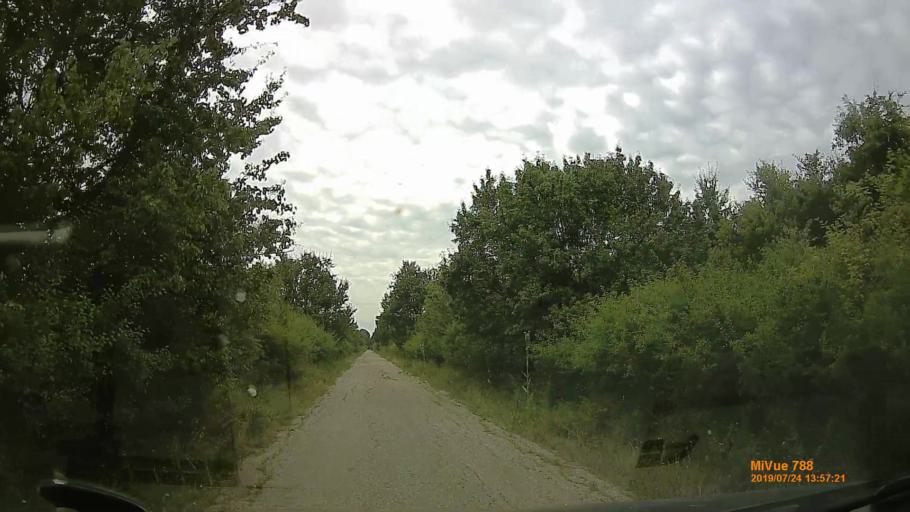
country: HU
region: Szabolcs-Szatmar-Bereg
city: Aranyosapati
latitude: 48.2624
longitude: 22.3297
